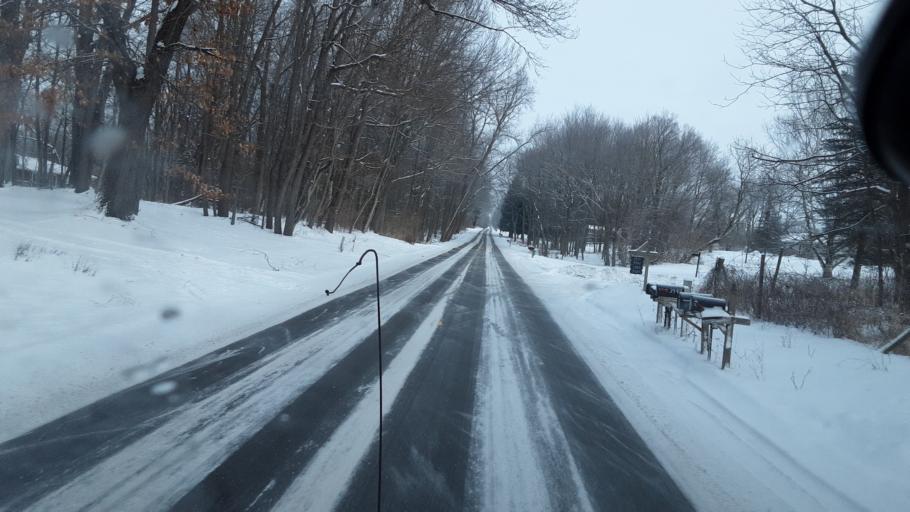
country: US
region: Michigan
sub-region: Jackson County
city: Jackson
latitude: 42.3112
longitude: -84.4829
